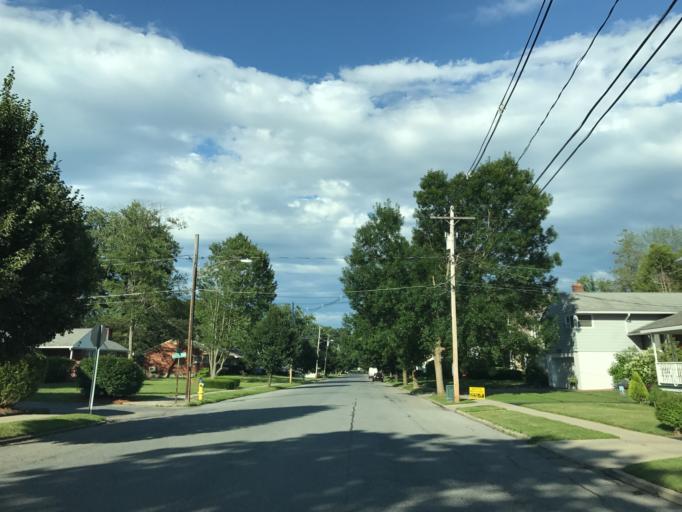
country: US
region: New York
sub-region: Warren County
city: Glens Falls
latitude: 43.3226
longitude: -73.6593
